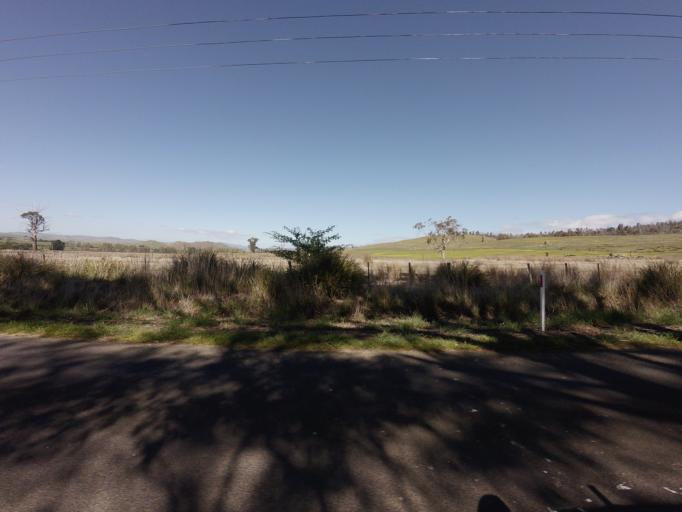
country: AU
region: Tasmania
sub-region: Derwent Valley
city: New Norfolk
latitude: -42.5377
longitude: 146.7235
